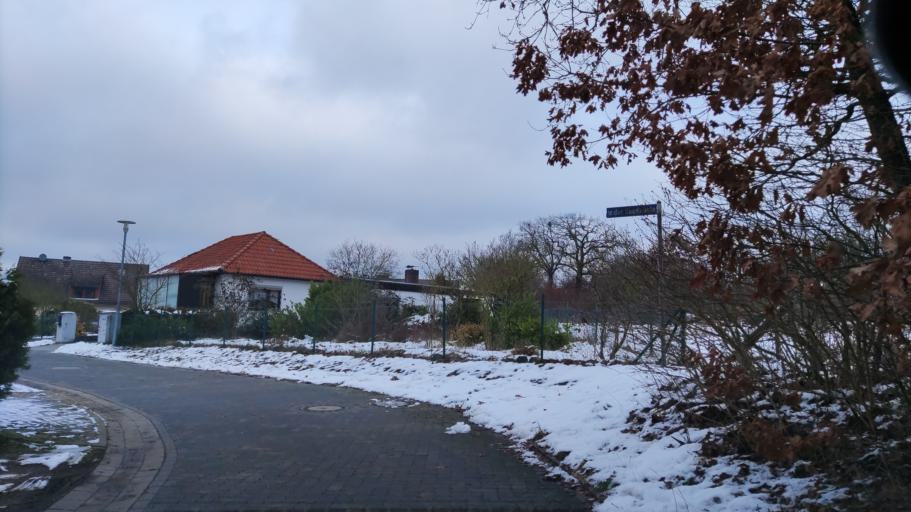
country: DE
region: Lower Saxony
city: Reinstorf
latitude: 53.2476
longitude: 10.5619
